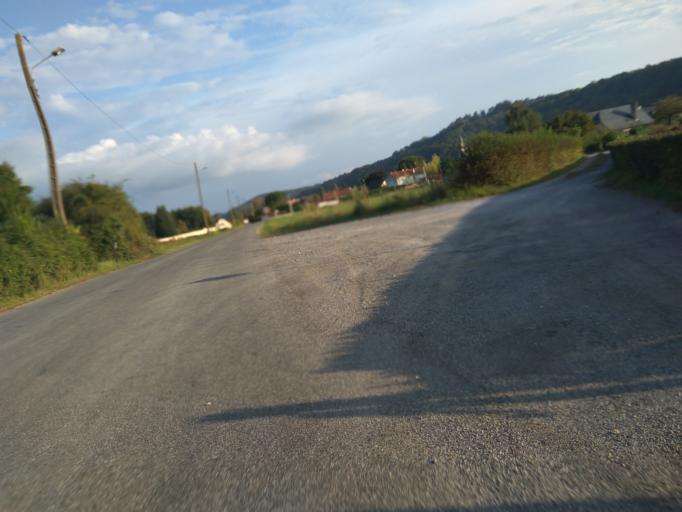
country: FR
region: Aquitaine
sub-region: Departement des Pyrenees-Atlantiques
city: Bizanos
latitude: 43.2798
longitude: -0.3525
